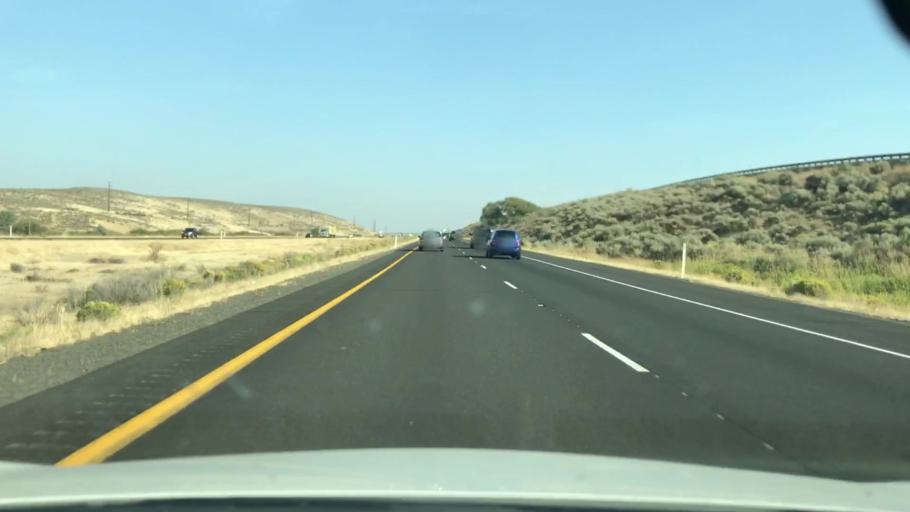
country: US
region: Washington
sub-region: Kittitas County
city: Kittitas
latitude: 46.9691
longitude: -120.3467
